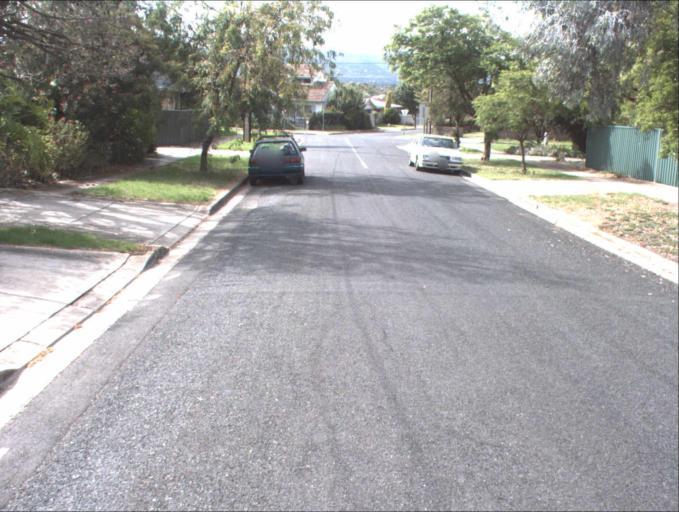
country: AU
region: South Australia
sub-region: Port Adelaide Enfield
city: Klemzig
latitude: -34.8801
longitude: 138.6320
